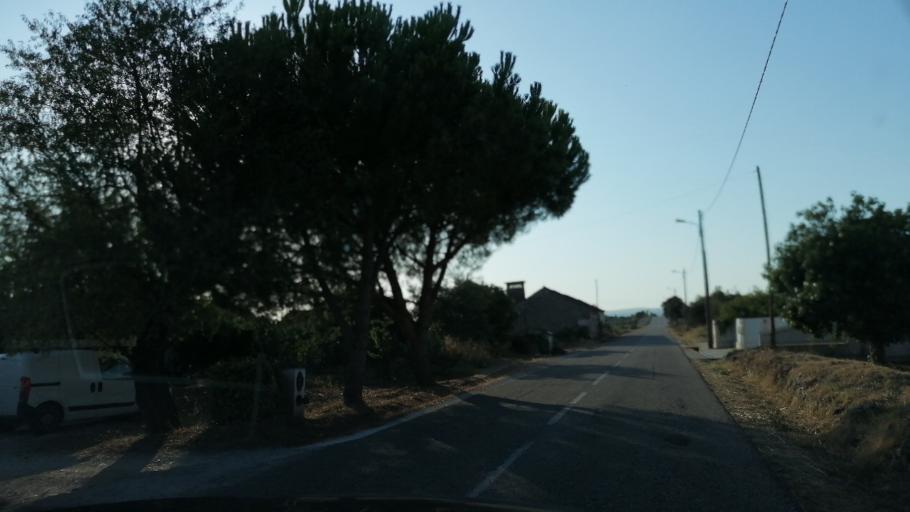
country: PT
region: Santarem
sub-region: Alcanena
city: Alcanena
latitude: 39.4524
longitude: -8.6250
